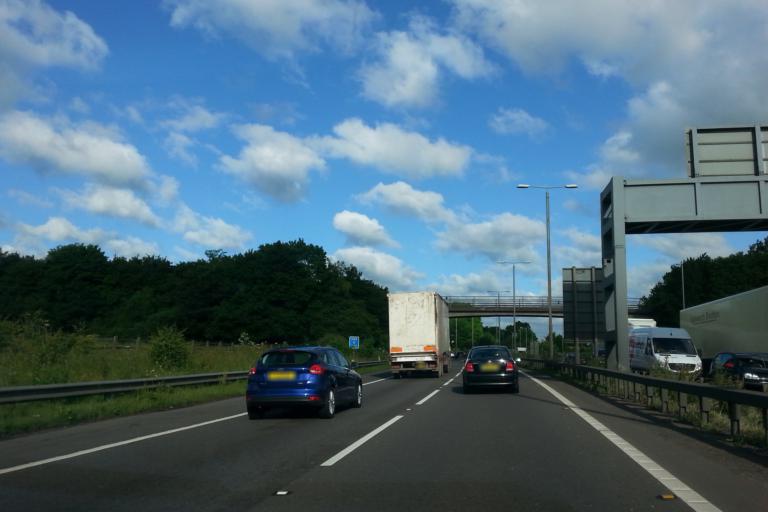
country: GB
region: England
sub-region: Leicestershire
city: Enderby
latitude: 52.6006
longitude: -1.1993
